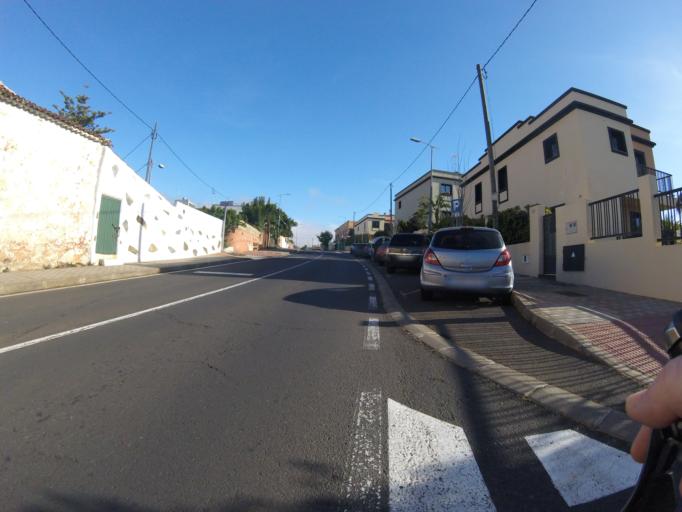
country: ES
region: Canary Islands
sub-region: Provincia de Santa Cruz de Tenerife
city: La Laguna
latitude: 28.4609
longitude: -16.3154
